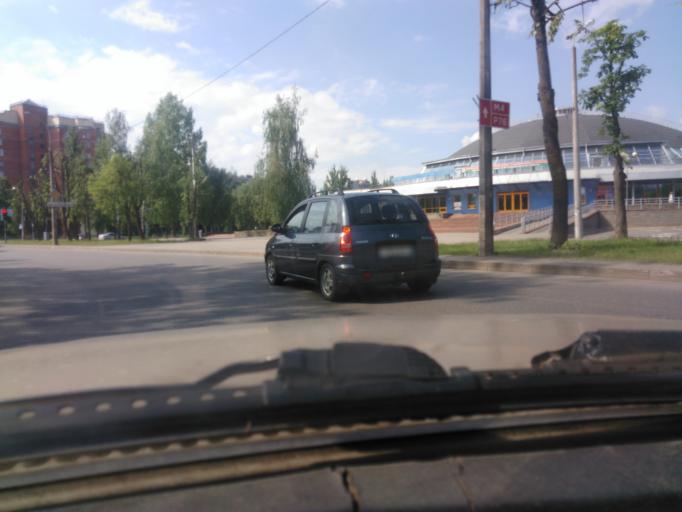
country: BY
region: Mogilev
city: Mahilyow
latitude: 53.9265
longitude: 30.3629
